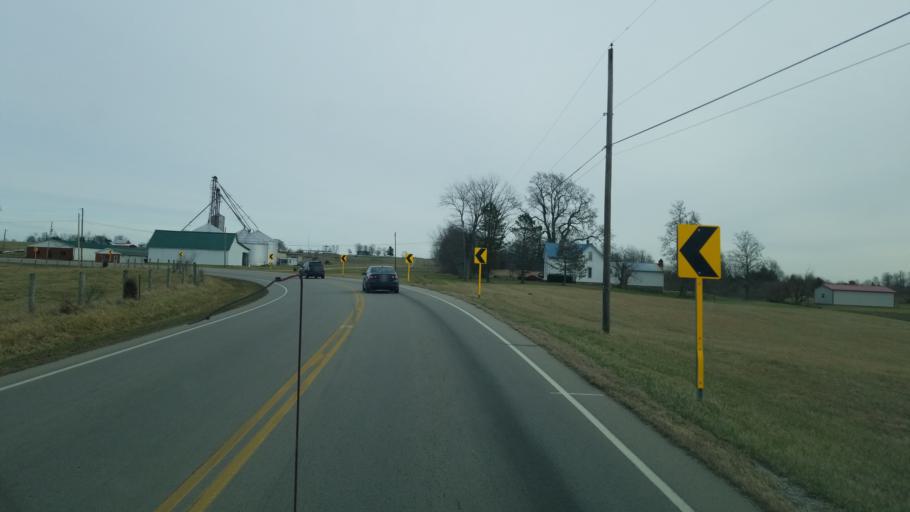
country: US
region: Ohio
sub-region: Adams County
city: Winchester
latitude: 39.0641
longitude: -83.6923
